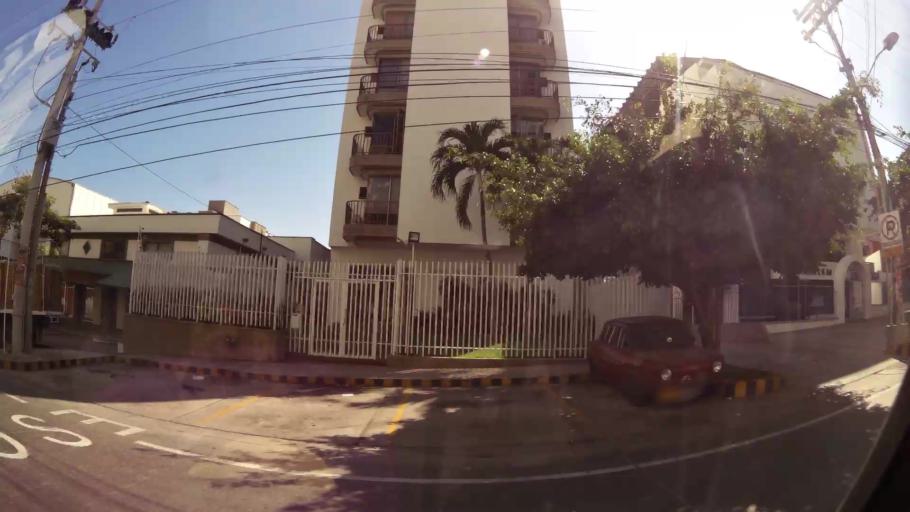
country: CO
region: Atlantico
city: Barranquilla
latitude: 11.0007
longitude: -74.8099
